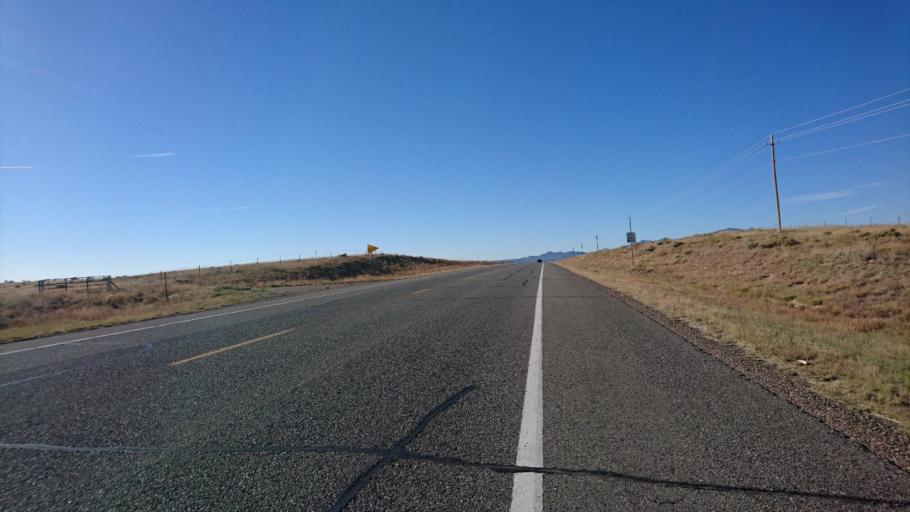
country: US
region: New Mexico
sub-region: Santa Fe County
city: La Cienega
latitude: 35.5112
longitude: -106.0618
